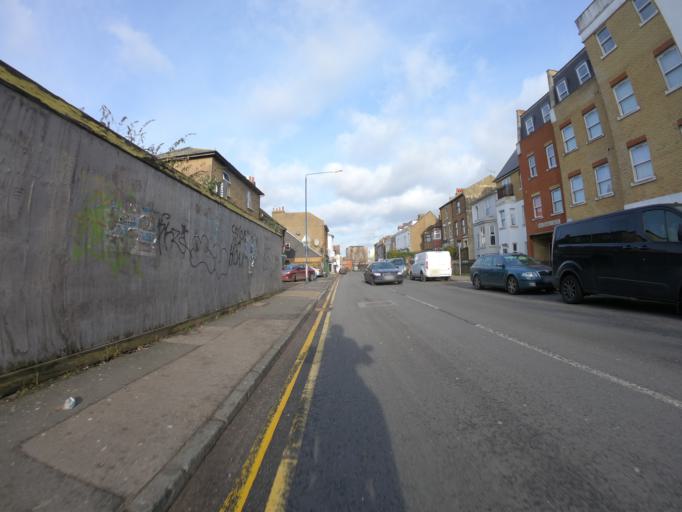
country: GB
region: England
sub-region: Kent
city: Gravesend
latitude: 51.4378
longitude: 0.3671
